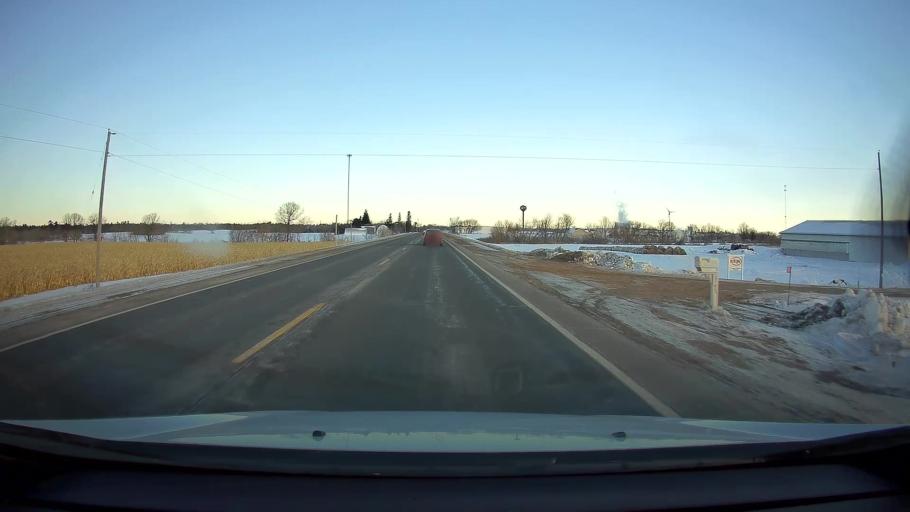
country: US
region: Wisconsin
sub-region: Barron County
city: Turtle Lake
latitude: 45.3831
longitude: -92.1667
